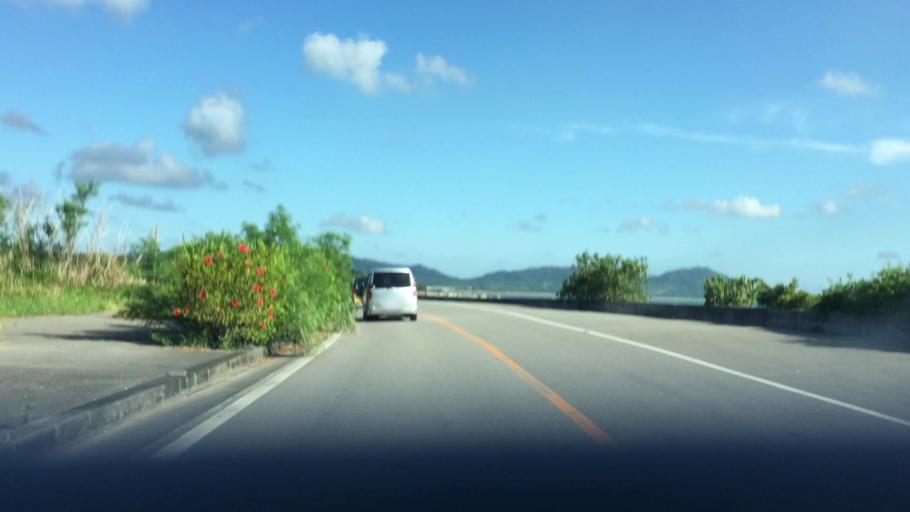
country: JP
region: Okinawa
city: Ishigaki
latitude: 24.4243
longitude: 124.1292
